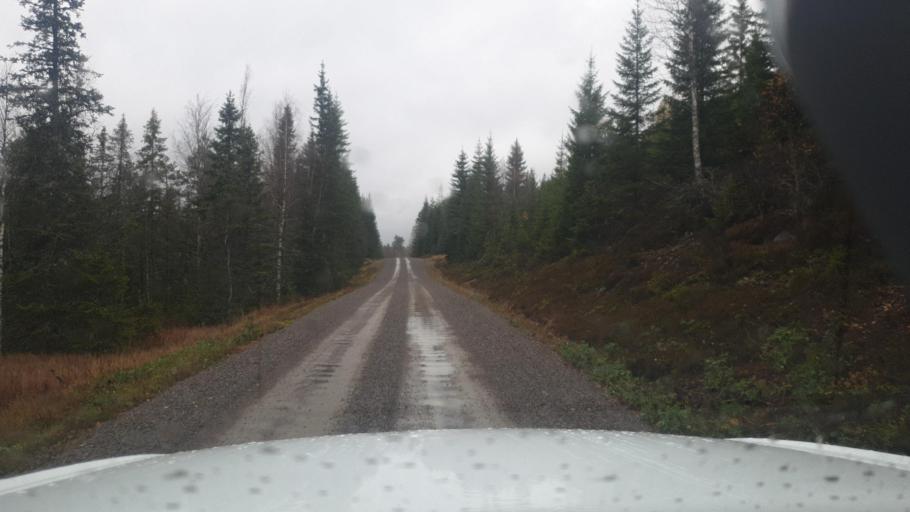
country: SE
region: Vaermland
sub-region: Eda Kommun
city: Charlottenberg
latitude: 60.1008
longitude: 12.6091
